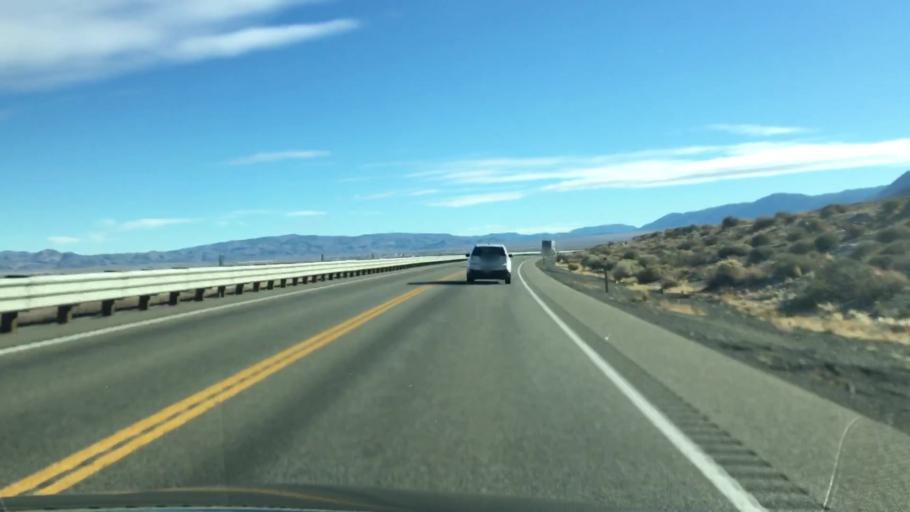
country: US
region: Nevada
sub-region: Mineral County
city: Hawthorne
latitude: 38.6074
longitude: -118.7134
